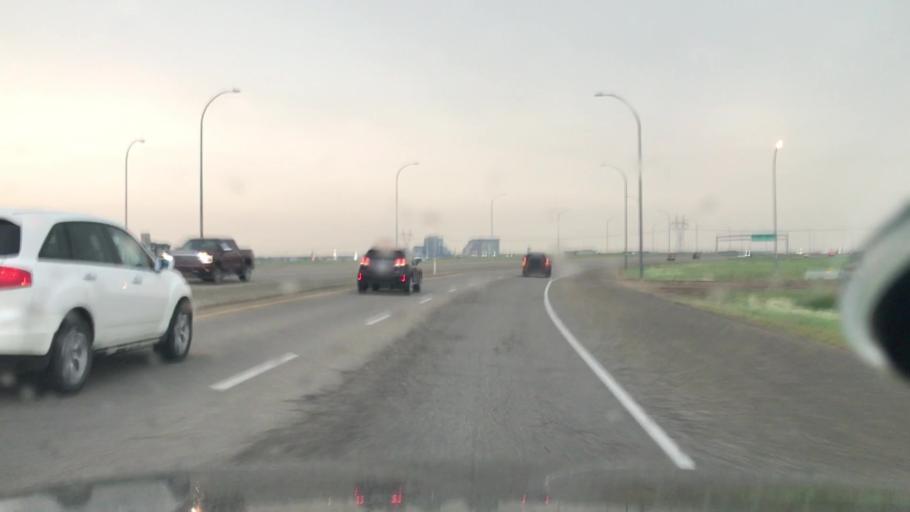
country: CA
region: Alberta
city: Edmonton
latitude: 53.4486
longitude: -113.5913
